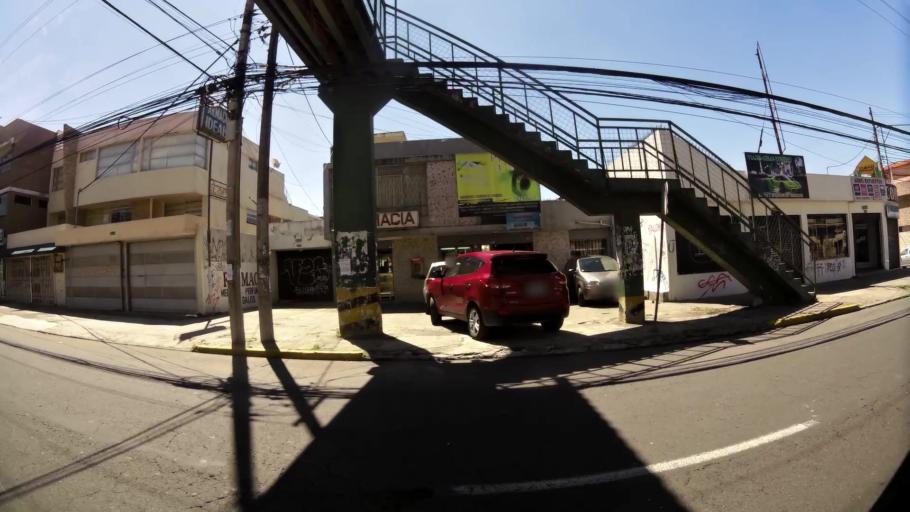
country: EC
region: Pichincha
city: Quito
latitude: -0.1470
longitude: -78.4910
